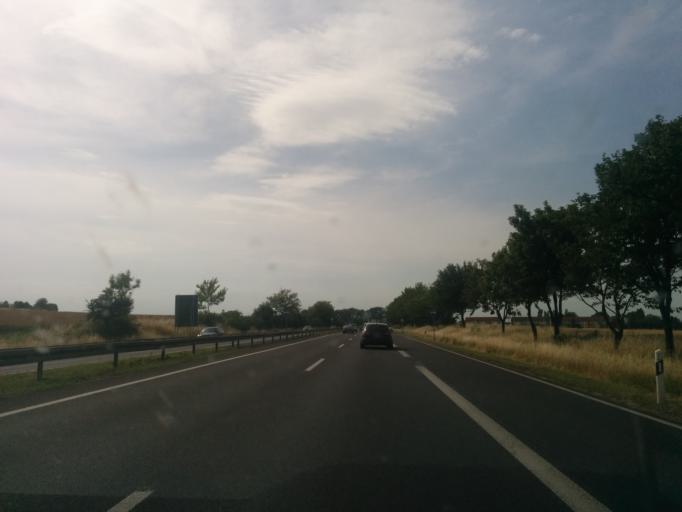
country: DE
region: Thuringia
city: Elxleben
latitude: 51.0355
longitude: 10.9557
